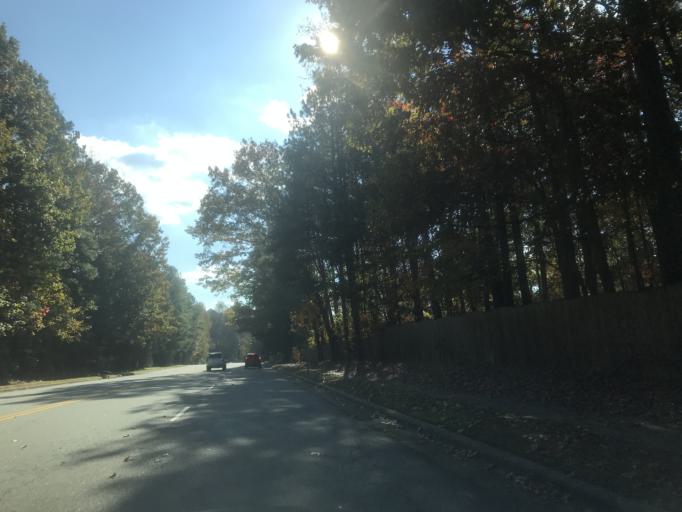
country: US
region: North Carolina
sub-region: Wake County
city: West Raleigh
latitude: 35.8956
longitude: -78.6631
